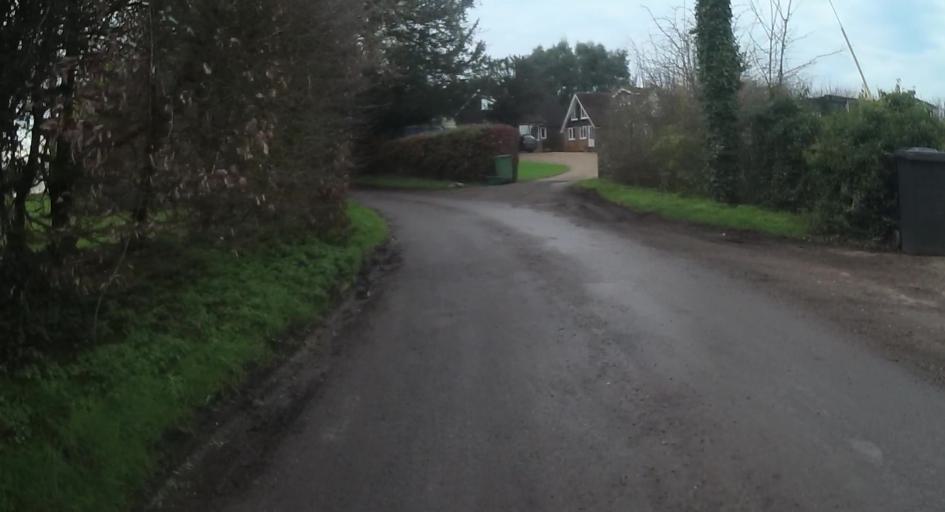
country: GB
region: England
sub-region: Hampshire
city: Kingsclere
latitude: 51.2883
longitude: -1.1865
